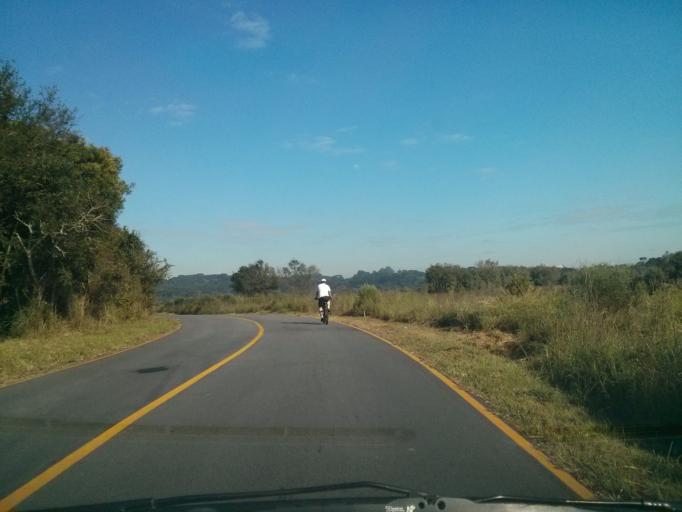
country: BR
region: Parana
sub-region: Sao Jose Dos Pinhais
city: Sao Jose dos Pinhais
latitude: -25.5426
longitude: -49.2243
